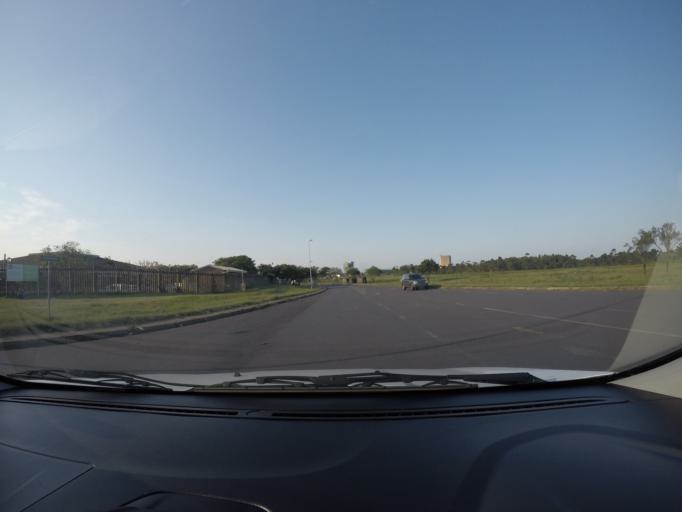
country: ZA
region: KwaZulu-Natal
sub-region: uThungulu District Municipality
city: Richards Bay
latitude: -28.7676
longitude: 32.0093
